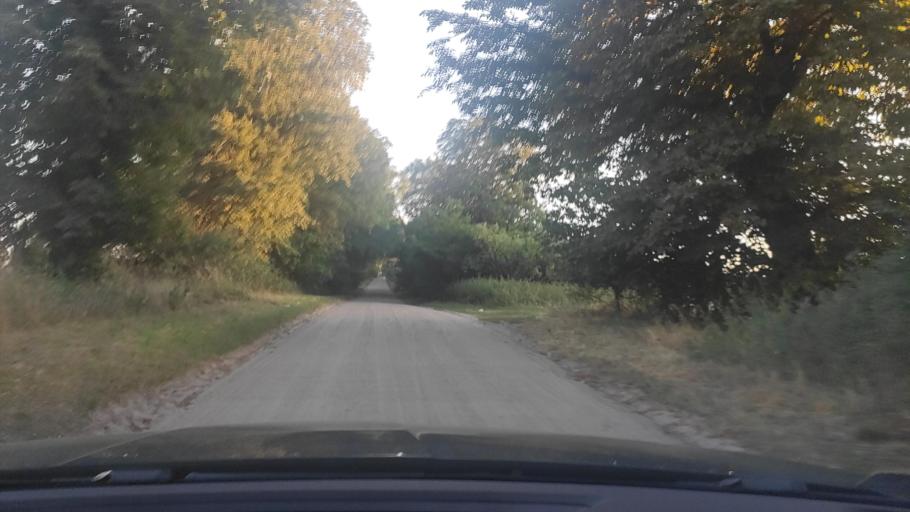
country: PL
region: Greater Poland Voivodeship
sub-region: Powiat poznanski
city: Swarzedz
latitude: 52.4400
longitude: 17.1238
